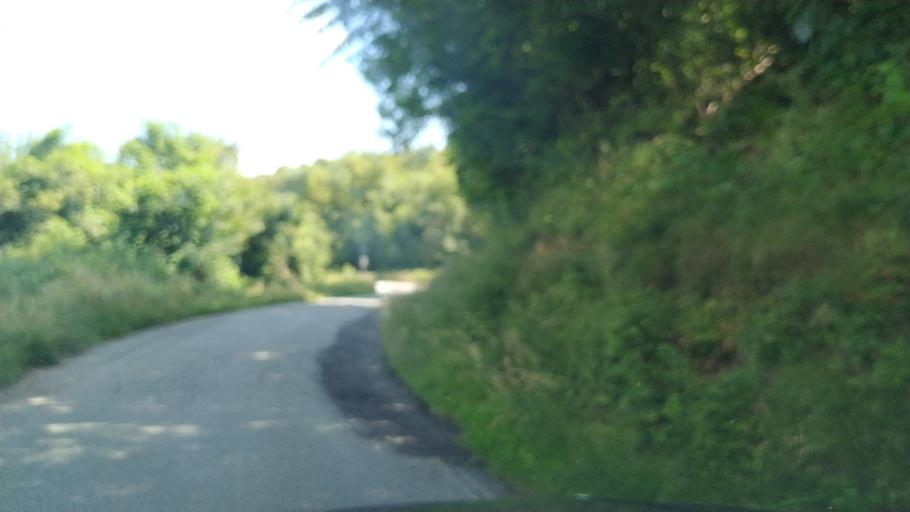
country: IT
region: Piedmont
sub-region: Provincia di Torino
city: Baldissero Canavese
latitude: 45.4108
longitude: 7.7189
